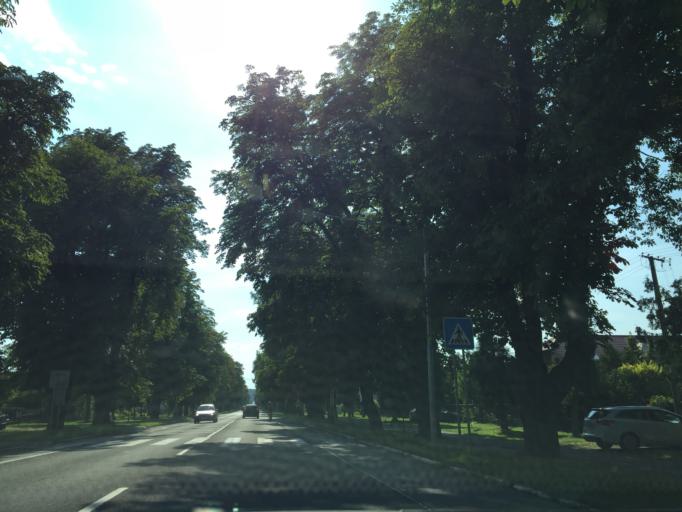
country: SK
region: Kosicky
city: Strazske
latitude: 48.8729
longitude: 21.8356
